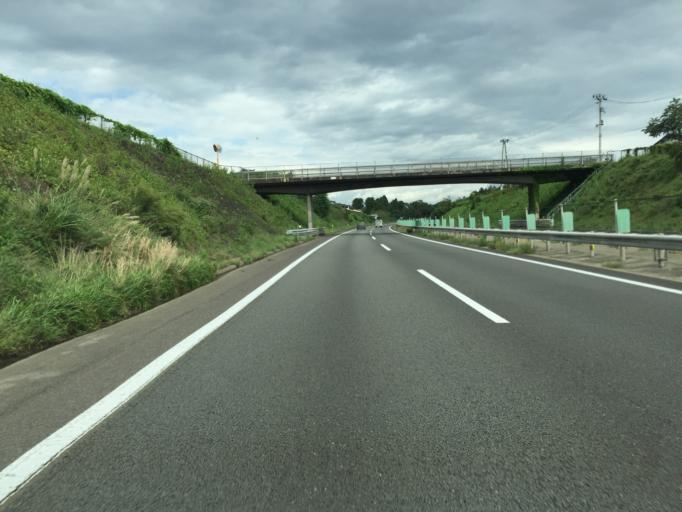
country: JP
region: Miyagi
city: Shiroishi
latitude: 38.0626
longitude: 140.6537
